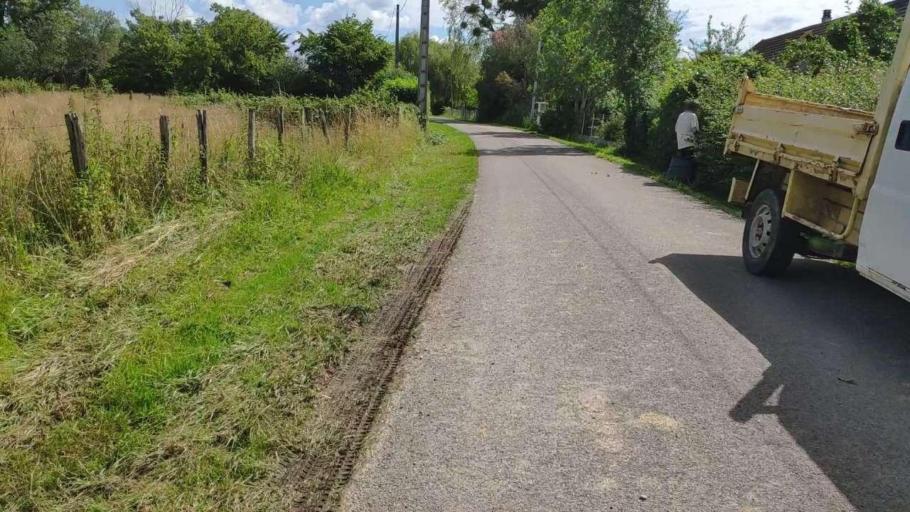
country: FR
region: Franche-Comte
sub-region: Departement du Jura
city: Bletterans
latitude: 46.8252
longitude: 5.4478
